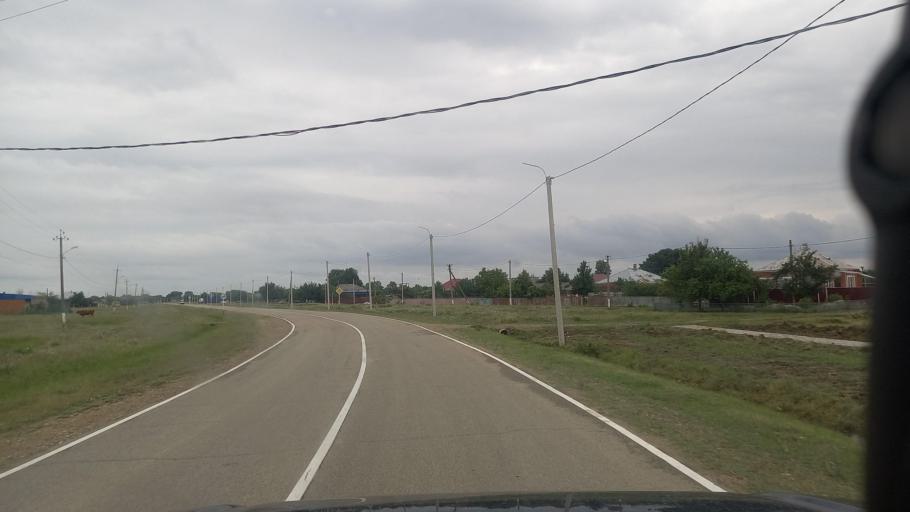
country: RU
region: Adygeya
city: Adygeysk
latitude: 44.8881
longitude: 39.2633
